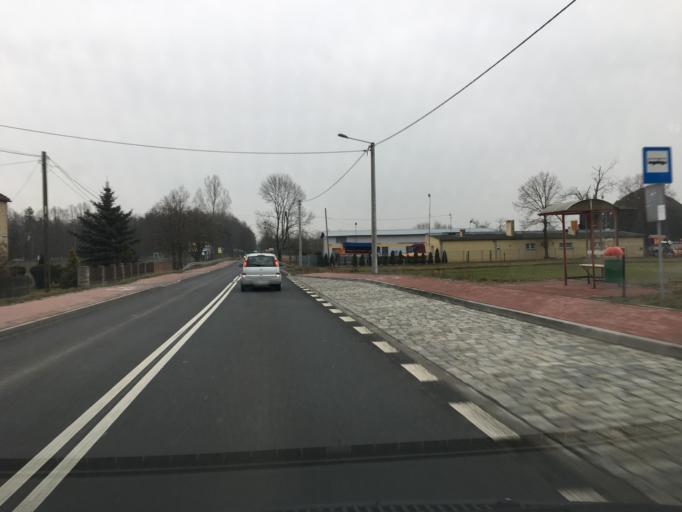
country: PL
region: Opole Voivodeship
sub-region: Powiat kedzierzynsko-kozielski
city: Bierawa
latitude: 50.3065
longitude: 18.2289
